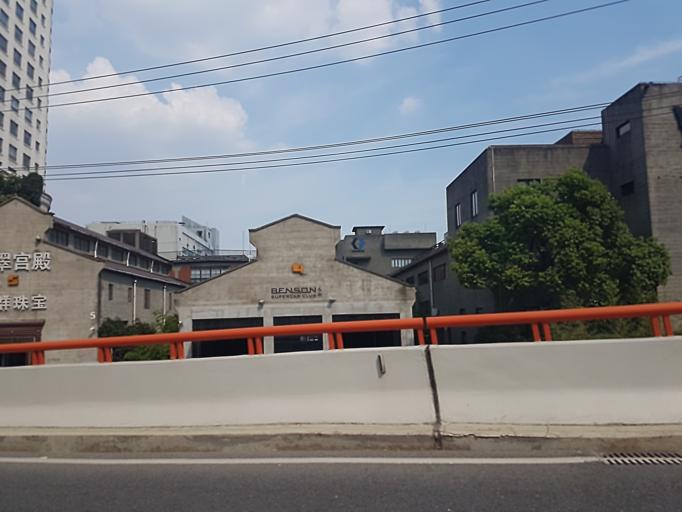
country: CN
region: Shanghai Shi
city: Pudong
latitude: 31.2136
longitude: 121.5005
